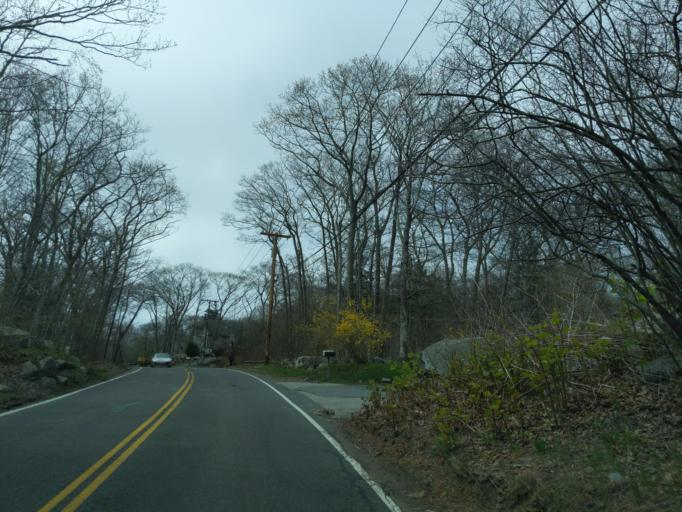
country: US
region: Massachusetts
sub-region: Essex County
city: Rockport
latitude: 42.6310
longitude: -70.6224
